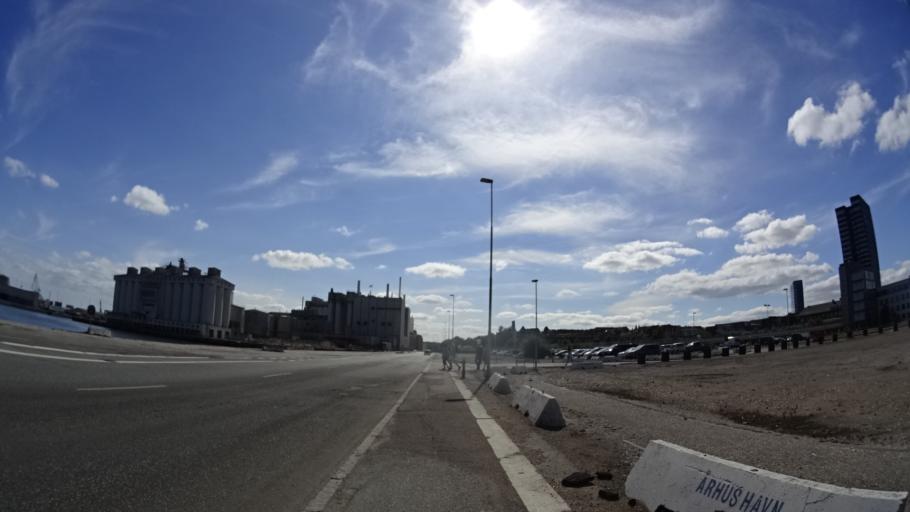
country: DK
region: Central Jutland
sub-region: Arhus Kommune
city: Arhus
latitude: 56.1504
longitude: 10.2149
